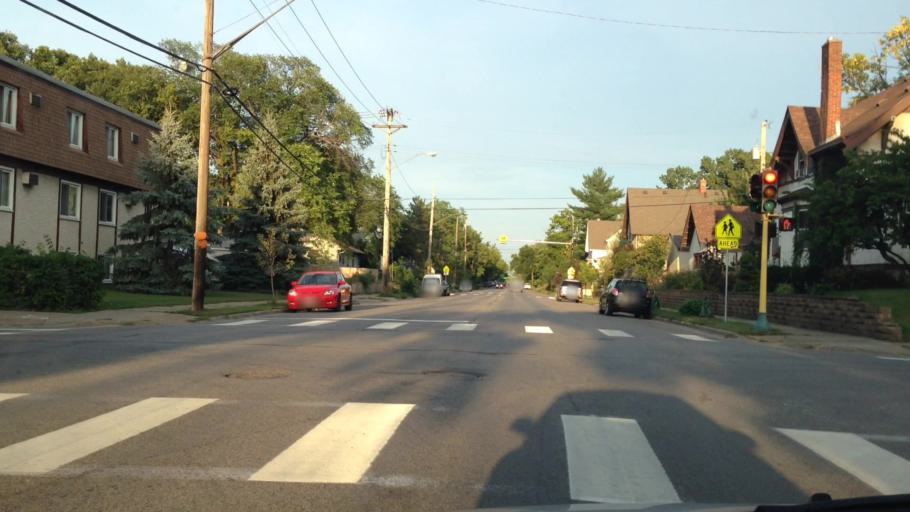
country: US
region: Minnesota
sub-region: Hennepin County
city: Minneapolis
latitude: 44.9377
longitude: -93.2846
